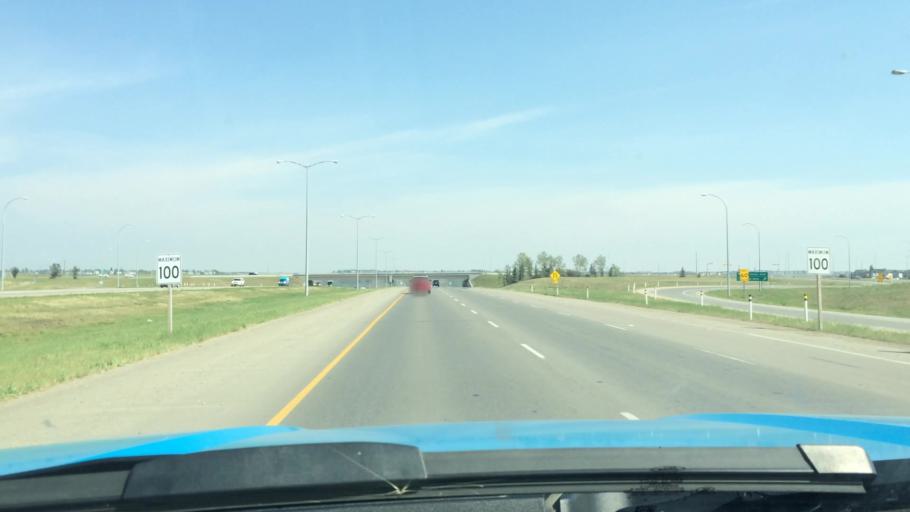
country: CA
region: Alberta
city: Calgary
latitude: 50.8926
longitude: -114.0321
